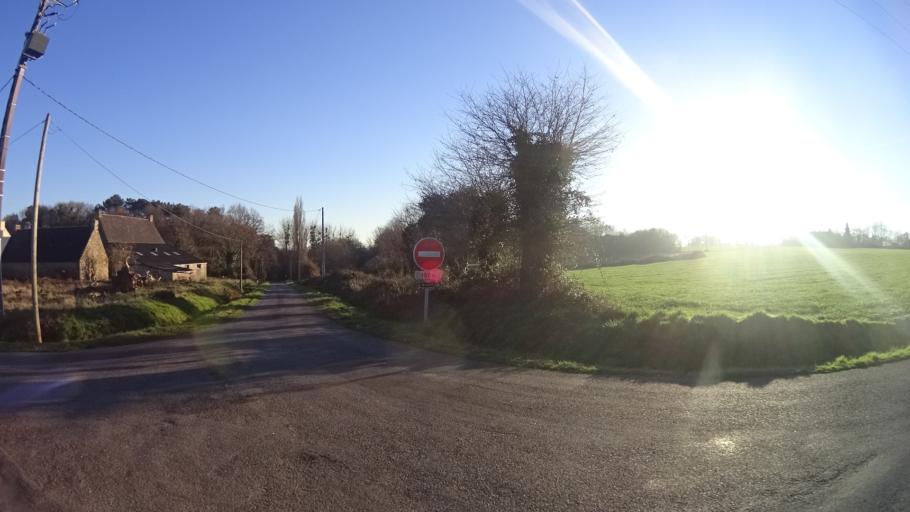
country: FR
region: Brittany
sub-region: Departement du Morbihan
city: Saint-Jean-la-Poterie
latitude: 47.6461
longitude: -2.1295
